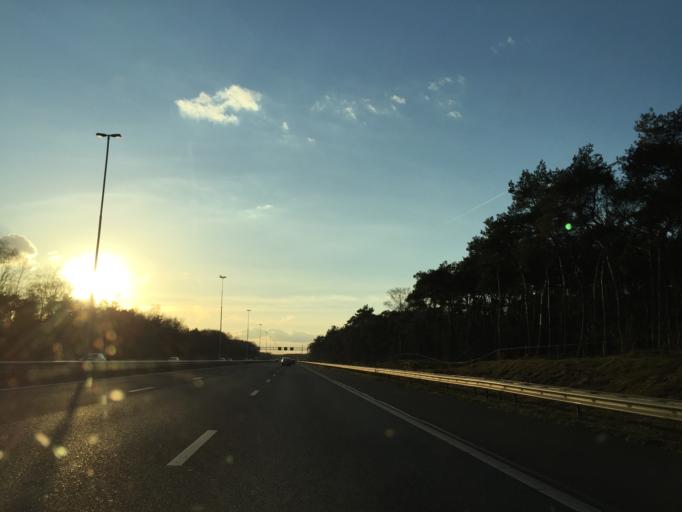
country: NL
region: North Brabant
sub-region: Gemeente Best
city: Best
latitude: 51.4882
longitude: 5.3785
